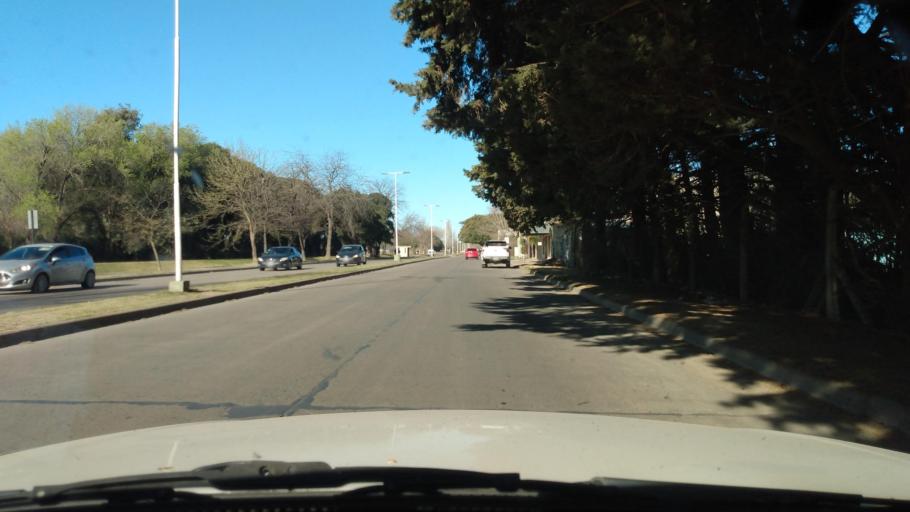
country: AR
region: Buenos Aires
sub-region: Partido de Mercedes
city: Mercedes
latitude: -34.6480
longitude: -59.4133
